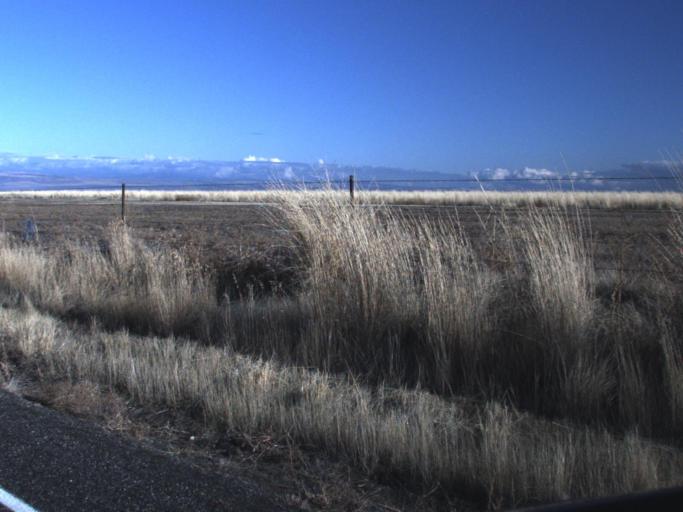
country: US
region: Washington
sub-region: Asotin County
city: Asotin
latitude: 46.2958
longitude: -117.0451
